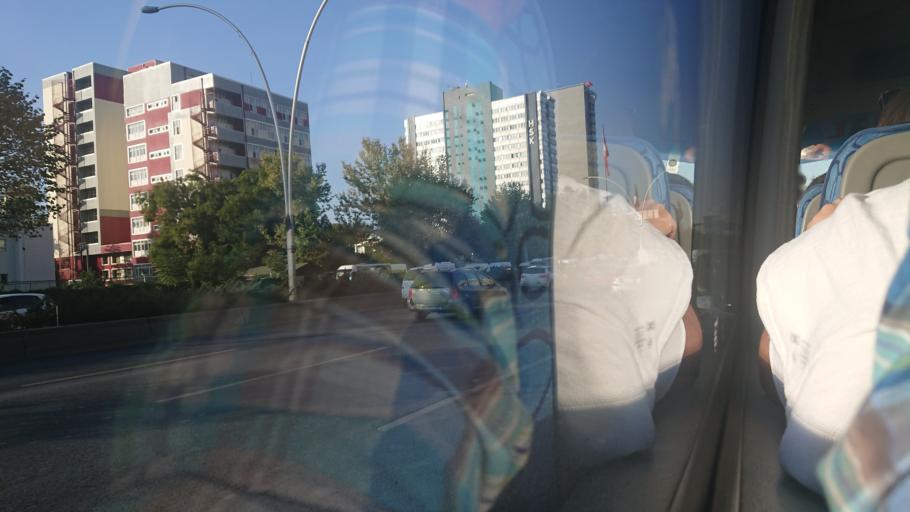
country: TR
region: Ankara
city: Ankara
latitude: 39.9384
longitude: 32.8242
